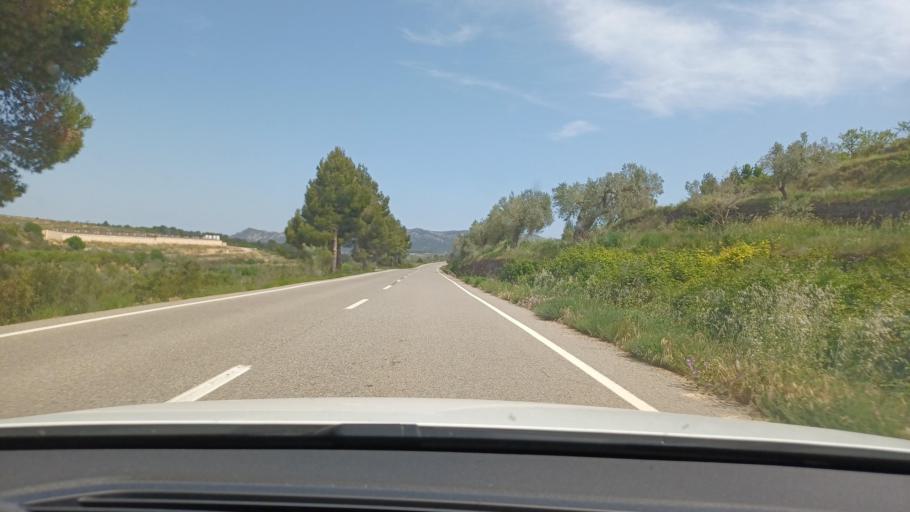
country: ES
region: Catalonia
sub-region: Provincia de Tarragona
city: Gandesa
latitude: 41.0796
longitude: 0.4236
